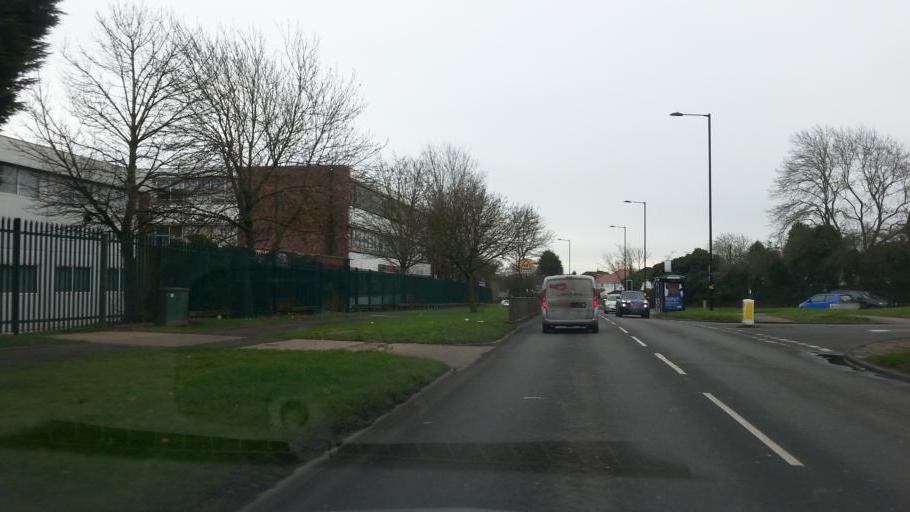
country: GB
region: England
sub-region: Solihull
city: Tidbury Green
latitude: 52.4049
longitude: -1.8924
